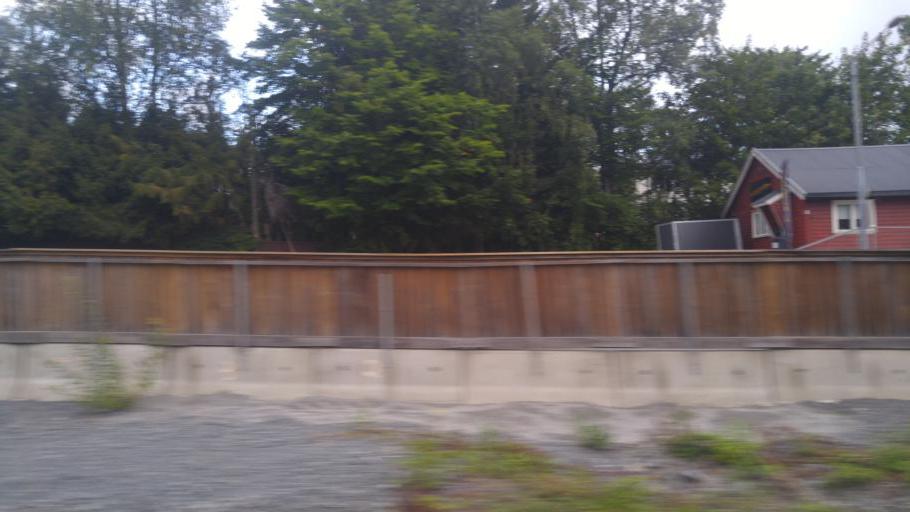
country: NO
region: Oslo
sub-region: Oslo
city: Sjolyststranda
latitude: 59.9503
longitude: 10.6951
